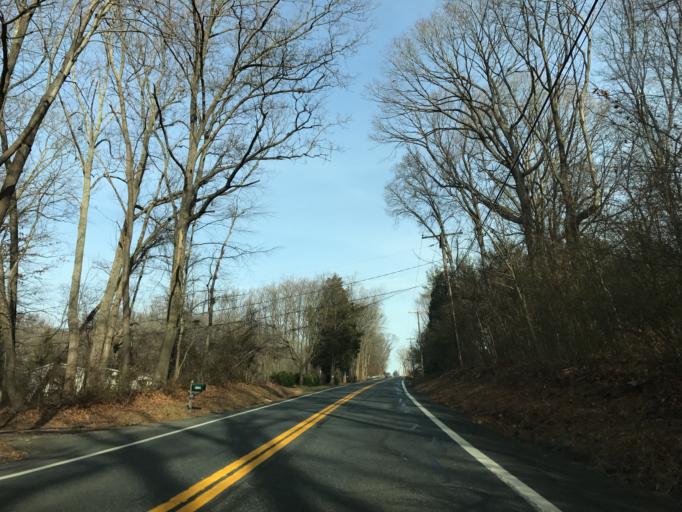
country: US
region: Maryland
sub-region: Harford County
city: Pleasant Hills
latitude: 39.4917
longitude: -76.4060
